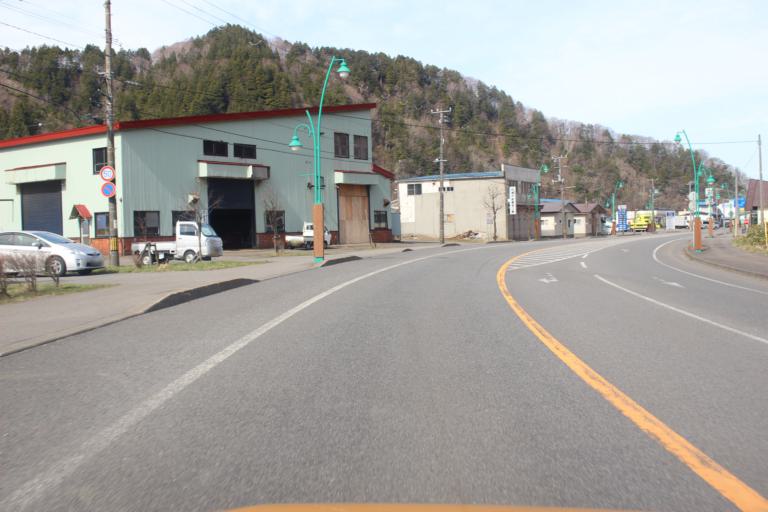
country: JP
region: Hokkaido
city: Kamiiso
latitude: 41.9140
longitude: 140.2299
